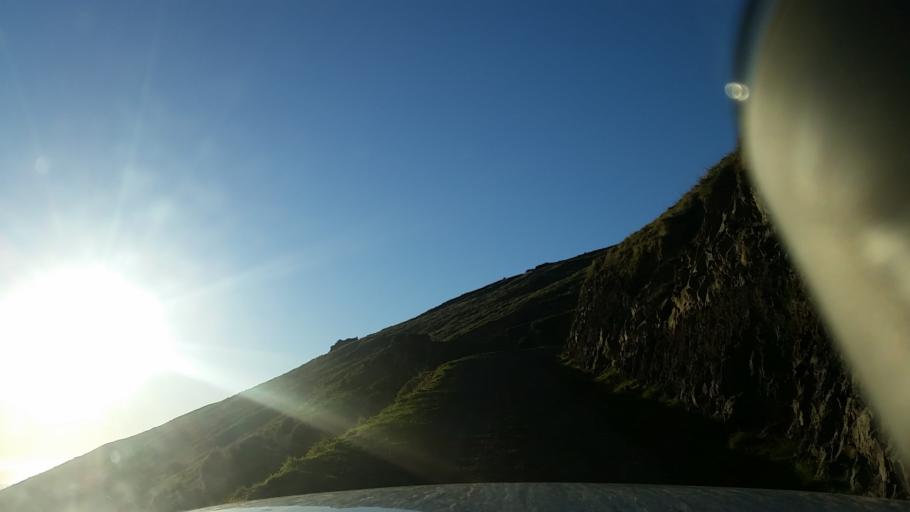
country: NZ
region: Canterbury
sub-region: Christchurch City
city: Christchurch
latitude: -43.7240
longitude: 173.0998
